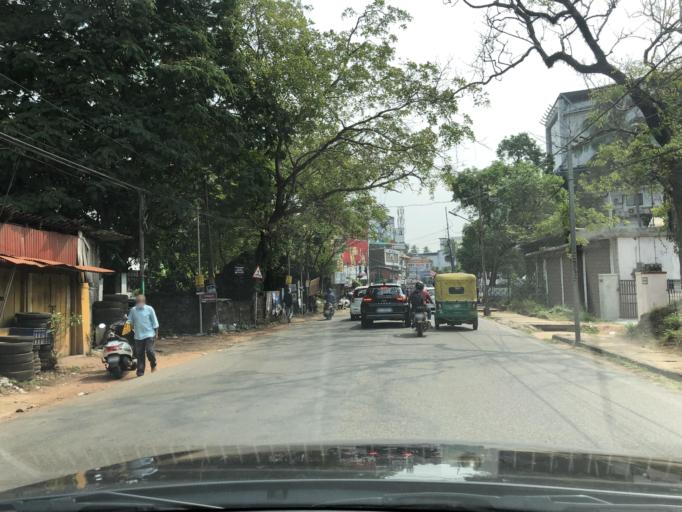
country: IN
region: Kerala
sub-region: Kozhikode
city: Kozhikode
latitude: 11.2656
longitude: 75.7791
